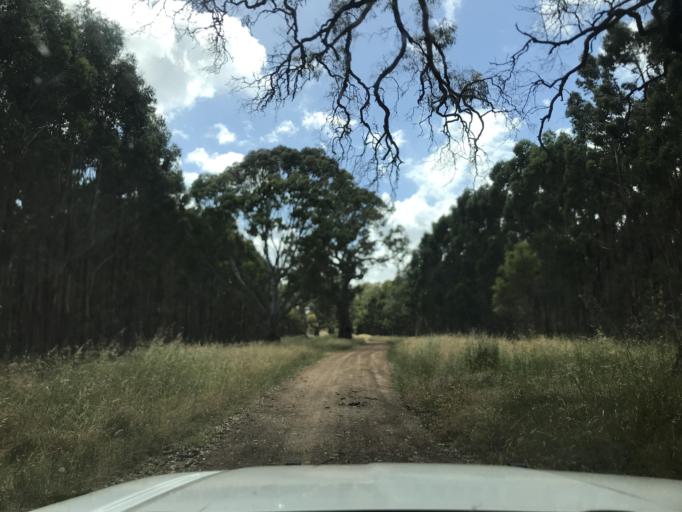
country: AU
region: South Australia
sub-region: Wattle Range
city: Penola
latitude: -37.1900
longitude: 141.3794
